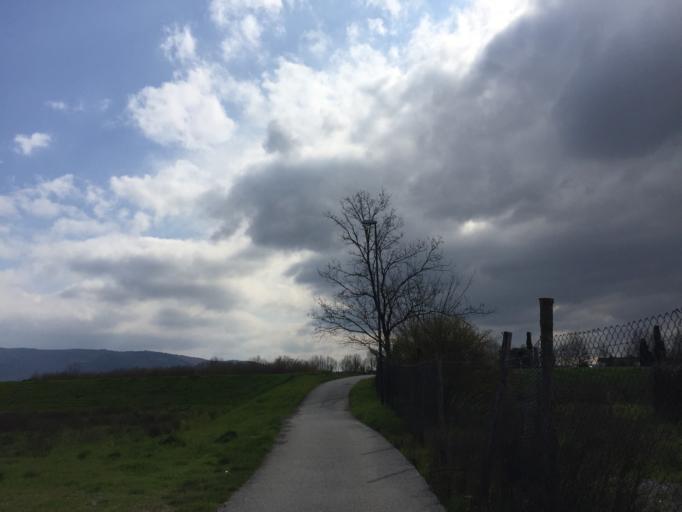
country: IT
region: Tuscany
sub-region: Provincia di Prato
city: Fornacelle
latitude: 43.8929
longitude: 11.0569
